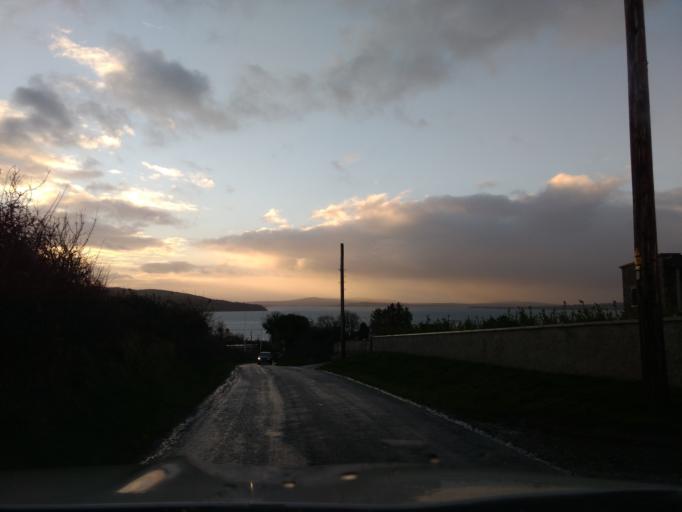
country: IE
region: Ulster
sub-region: County Donegal
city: Buncrana
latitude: 55.0964
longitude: -7.5423
